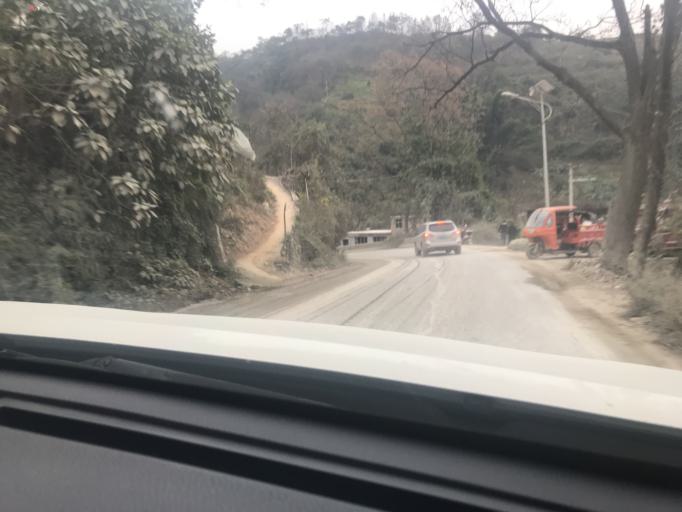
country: CN
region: Guangxi Zhuangzu Zizhiqu
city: Xinzhou
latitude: 24.9859
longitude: 105.8213
